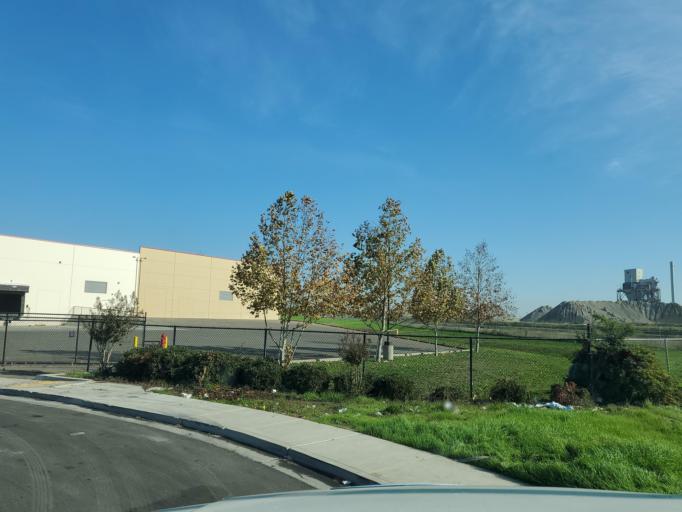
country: US
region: California
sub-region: San Joaquin County
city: Kennedy
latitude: 37.9345
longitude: -121.2231
